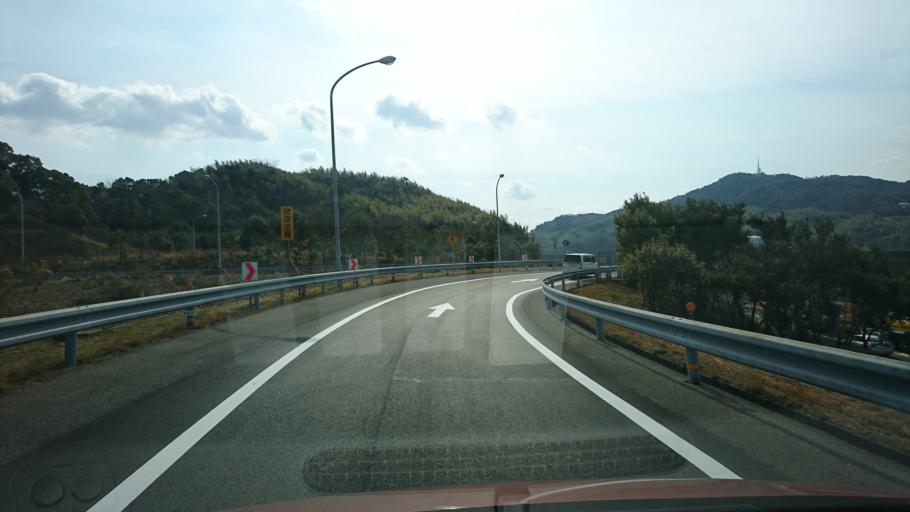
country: JP
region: Ehime
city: Hojo
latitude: 34.0993
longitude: 132.9781
